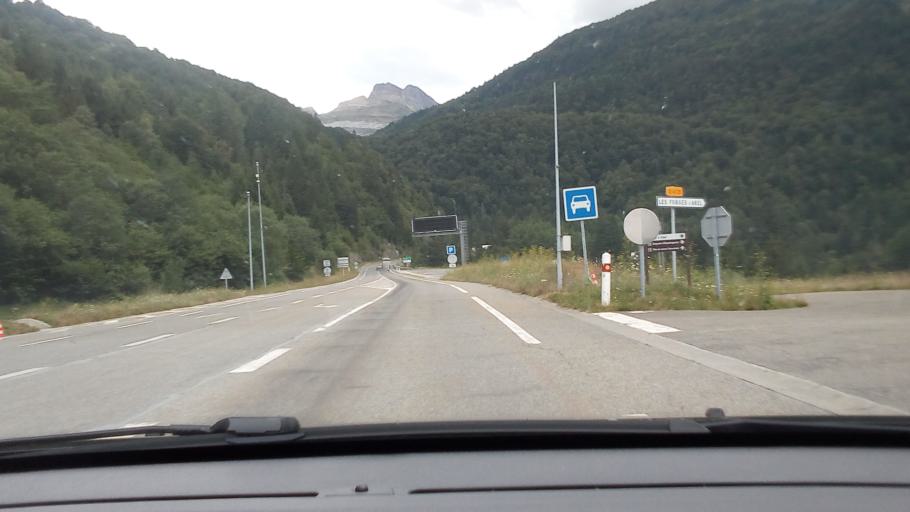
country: ES
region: Aragon
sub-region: Provincia de Huesca
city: Canfranc
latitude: 42.8223
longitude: -0.5592
